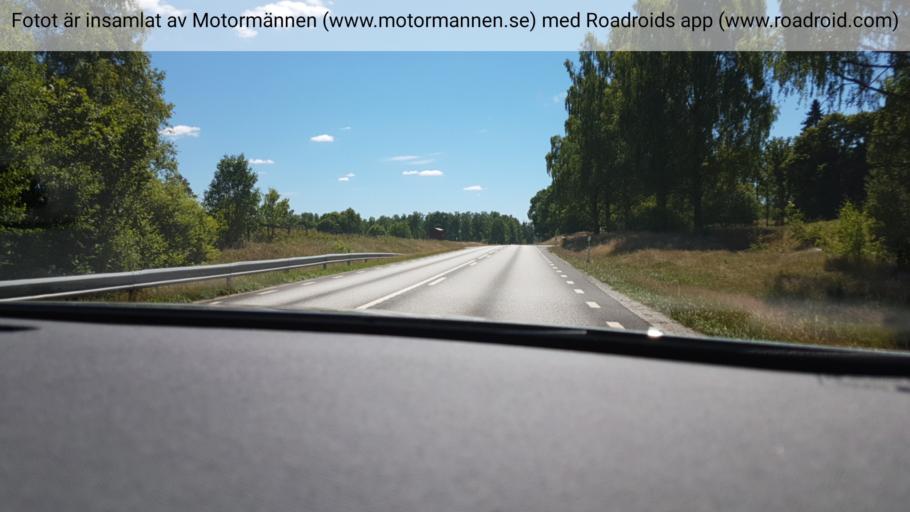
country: SE
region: Joenkoeping
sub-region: Gnosjo Kommun
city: Gnosjoe
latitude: 57.5398
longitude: 13.6890
